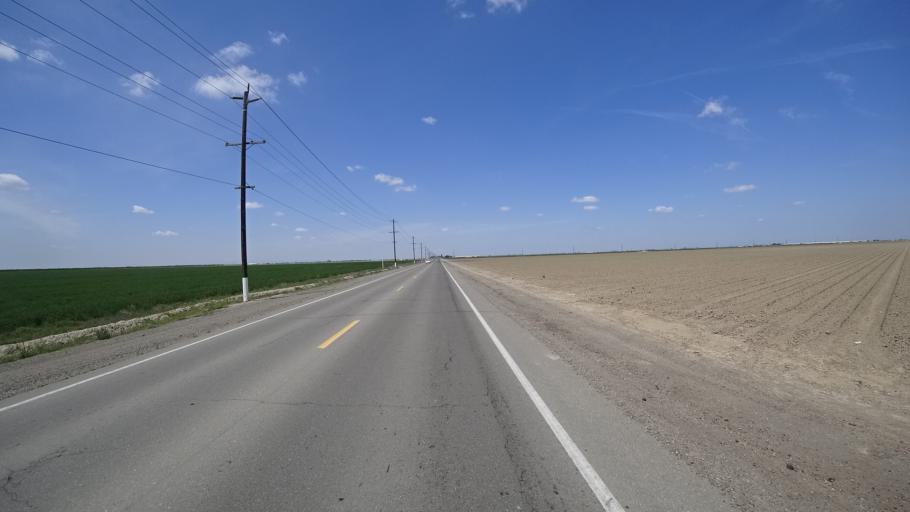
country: US
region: California
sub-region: Tulare County
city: Goshen
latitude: 36.2980
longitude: -119.4960
